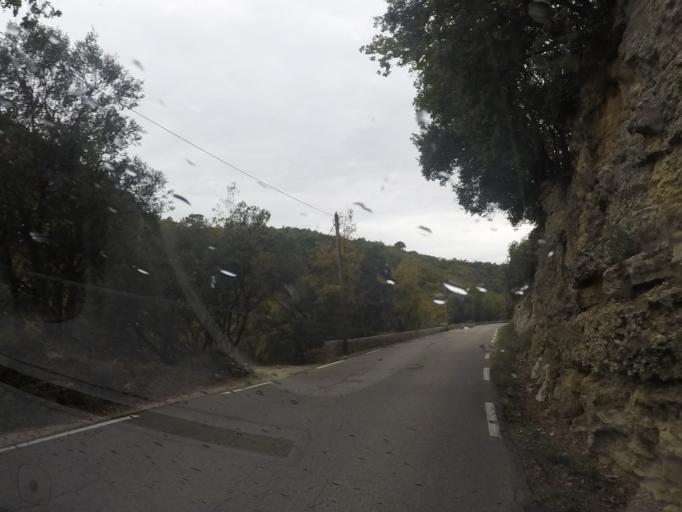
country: FR
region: Provence-Alpes-Cote d'Azur
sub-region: Departement du Vaucluse
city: Bonnieux
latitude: 43.8125
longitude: 5.3390
